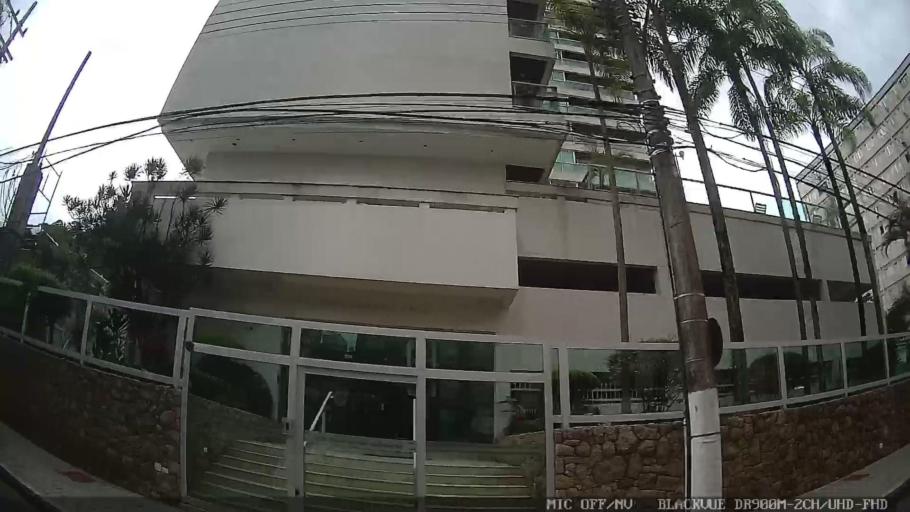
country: BR
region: Sao Paulo
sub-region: Guaruja
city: Guaruja
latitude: -23.9967
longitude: -46.2607
